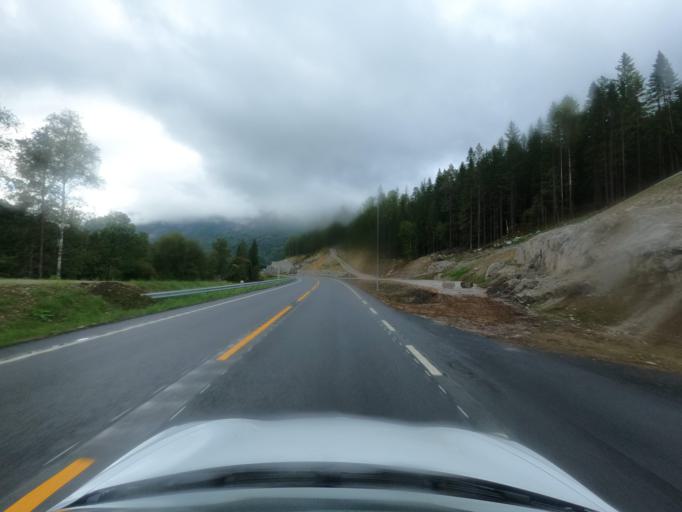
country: NO
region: Telemark
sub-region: Seljord
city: Seljord
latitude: 59.5073
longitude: 8.6455
